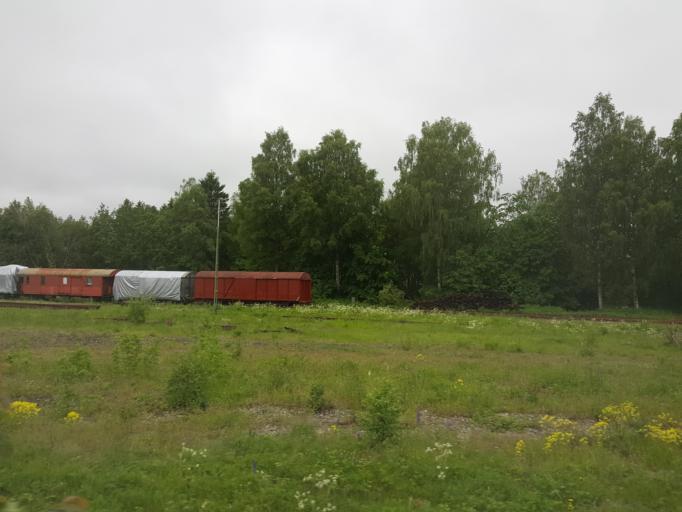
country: SE
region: Dalarna
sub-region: Avesta Kommun
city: Avesta
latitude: 60.1238
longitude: 16.2209
